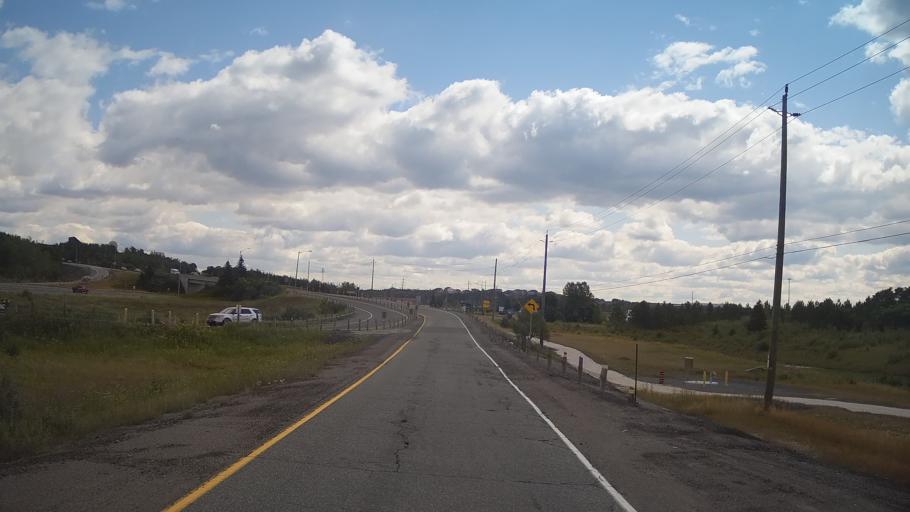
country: CA
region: Ontario
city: Greater Sudbury
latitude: 46.4719
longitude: -81.0432
